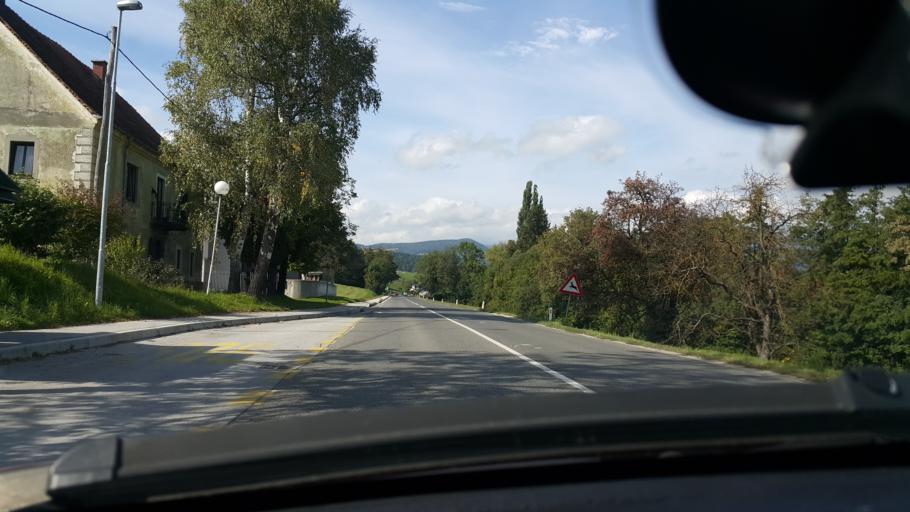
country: SI
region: Slovenska Konjice
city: Slovenske Konjice
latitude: 46.3464
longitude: 15.4082
